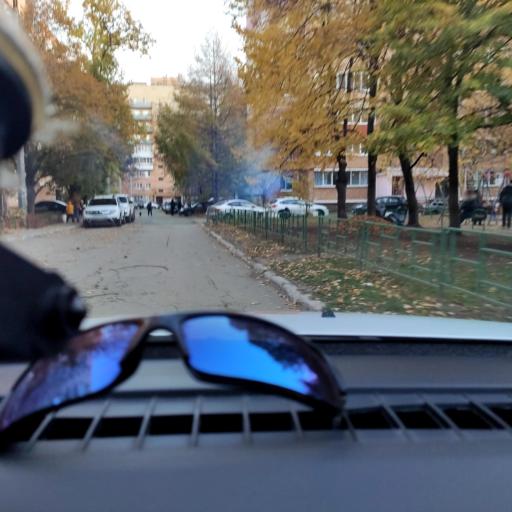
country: RU
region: Samara
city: Samara
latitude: 53.2356
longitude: 50.2504
